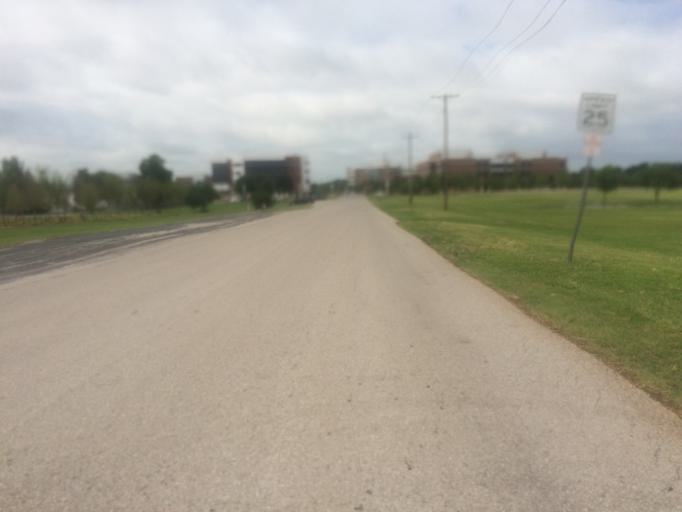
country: US
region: Oklahoma
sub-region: Cleveland County
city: Norman
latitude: 35.1889
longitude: -97.4397
